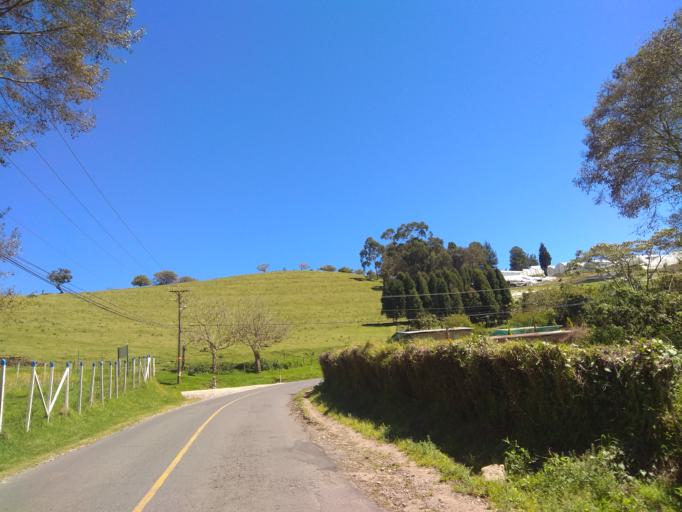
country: CR
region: Cartago
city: Cot
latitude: 9.9443
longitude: -83.9202
